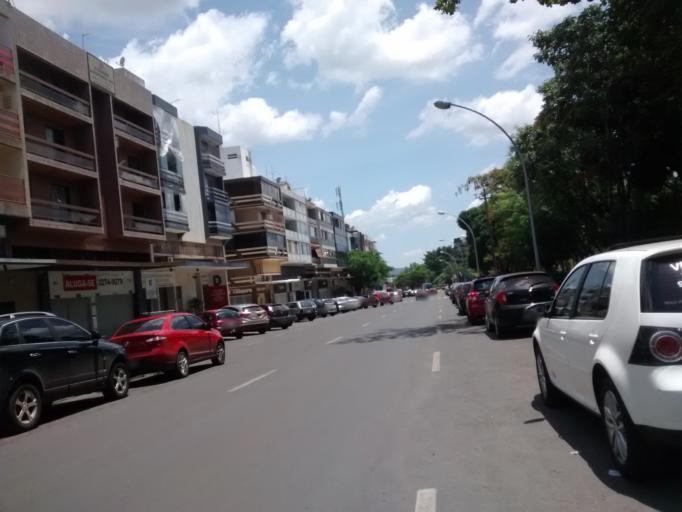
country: BR
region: Federal District
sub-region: Brasilia
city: Brasilia
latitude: -15.7582
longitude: -47.8953
